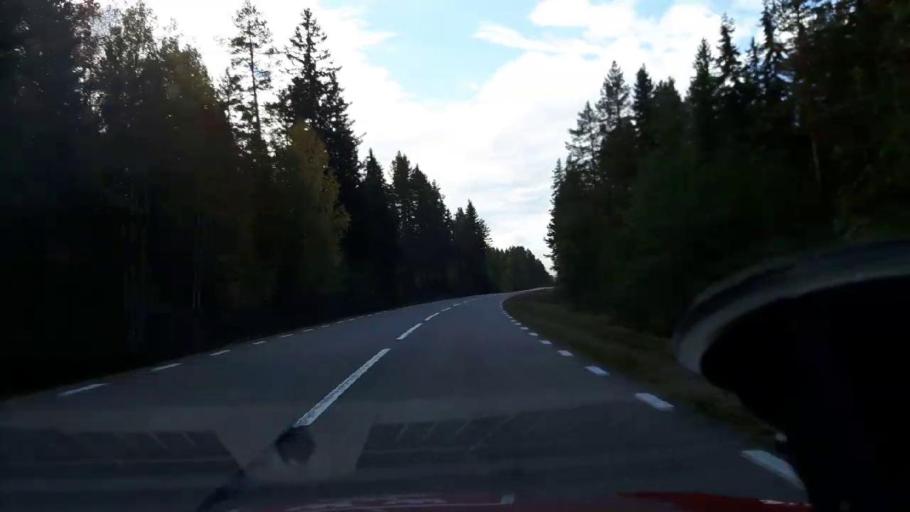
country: SE
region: Gaevleborg
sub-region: Ljusdals Kommun
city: Farila
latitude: 62.0139
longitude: 15.2405
